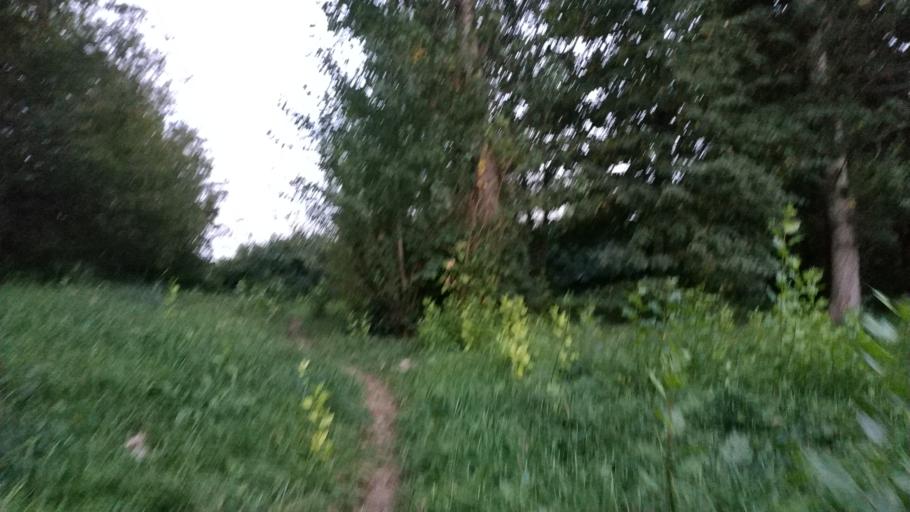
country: RU
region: Moscow
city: Solntsevo
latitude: 55.6363
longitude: 37.3783
